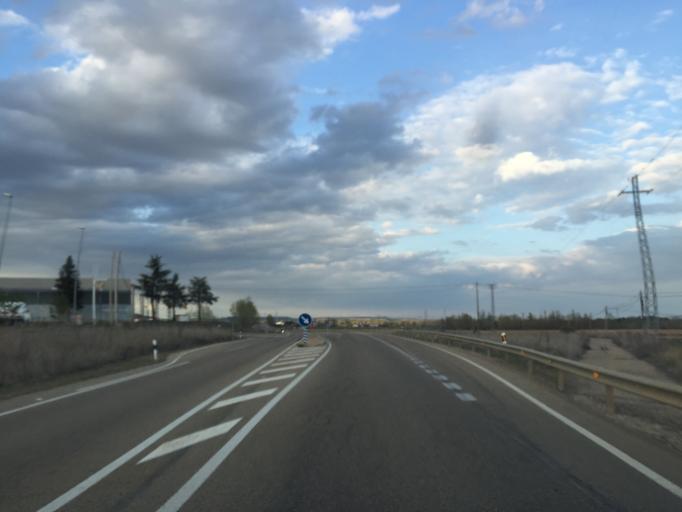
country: ES
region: Castille and Leon
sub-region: Provincia de Palencia
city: Soto de Cerrato
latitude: 41.9585
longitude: -4.4516
